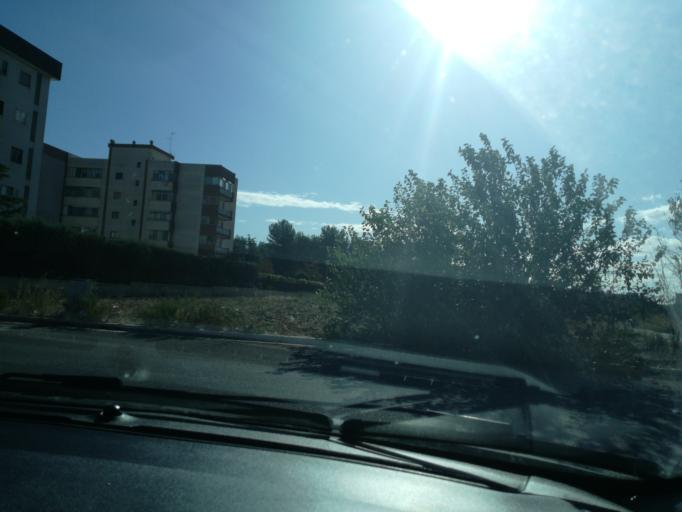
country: IT
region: Apulia
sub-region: Provincia di Bari
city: Triggiano
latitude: 41.0707
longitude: 16.9272
